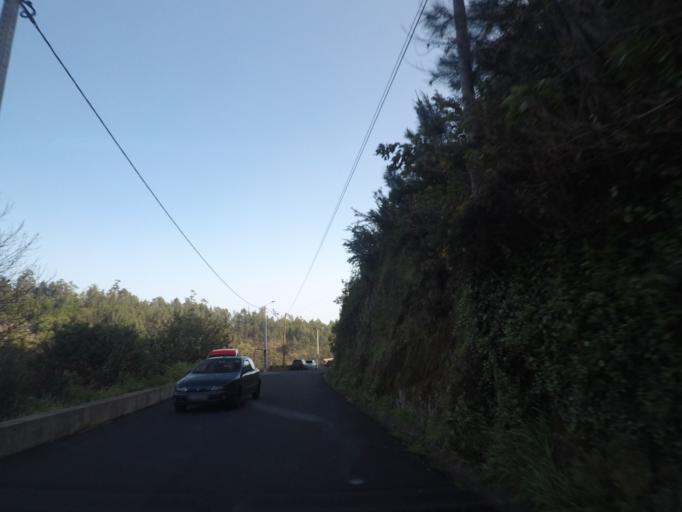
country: PT
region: Madeira
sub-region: Ribeira Brava
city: Campanario
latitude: 32.6762
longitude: -17.0062
